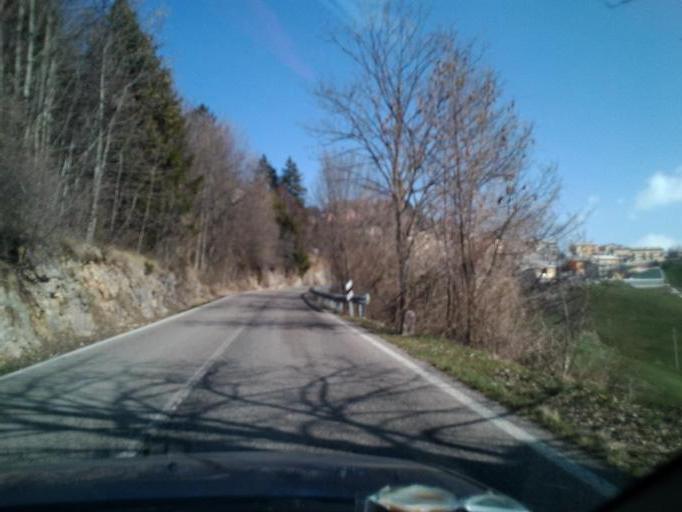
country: IT
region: Veneto
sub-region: Provincia di Verona
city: Bosco Chiesanuova
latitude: 45.6160
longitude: 11.0310
